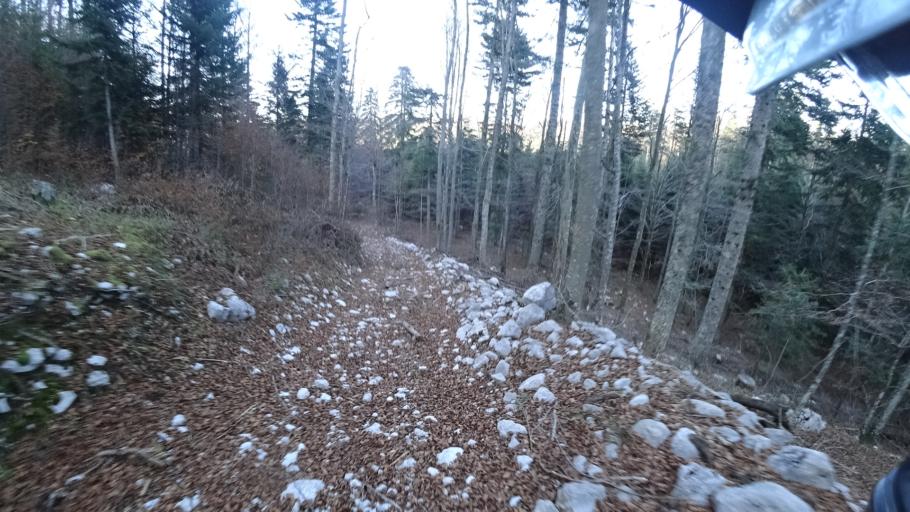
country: HR
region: Primorsko-Goranska
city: Klana
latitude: 45.4844
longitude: 14.4583
